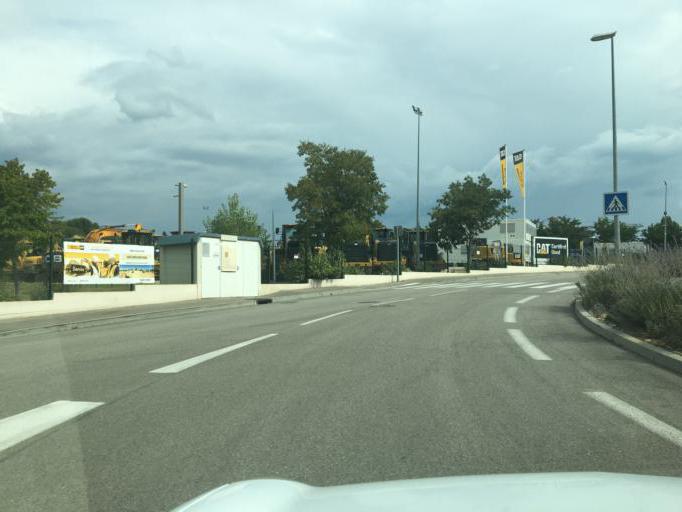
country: FR
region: Provence-Alpes-Cote d'Azur
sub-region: Departement des Bouches-du-Rhone
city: Bouc-Bel-Air
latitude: 43.4871
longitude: 5.3877
